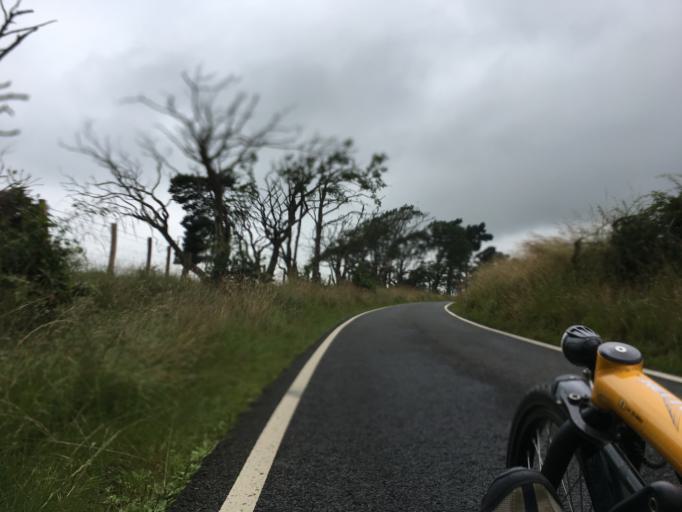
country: GB
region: Scotland
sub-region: West Lothian
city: West Calder
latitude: 55.8450
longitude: -3.5299
